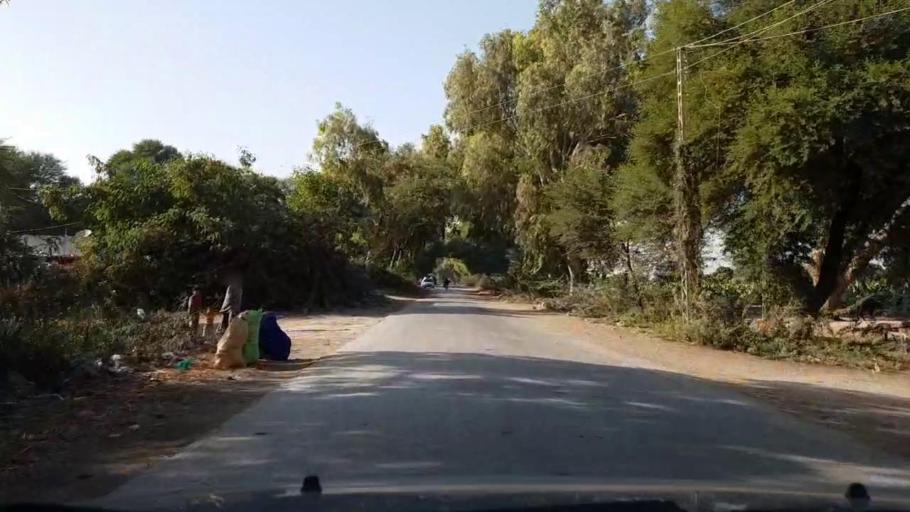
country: PK
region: Sindh
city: Tando Ghulam Ali
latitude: 25.1297
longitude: 68.8858
